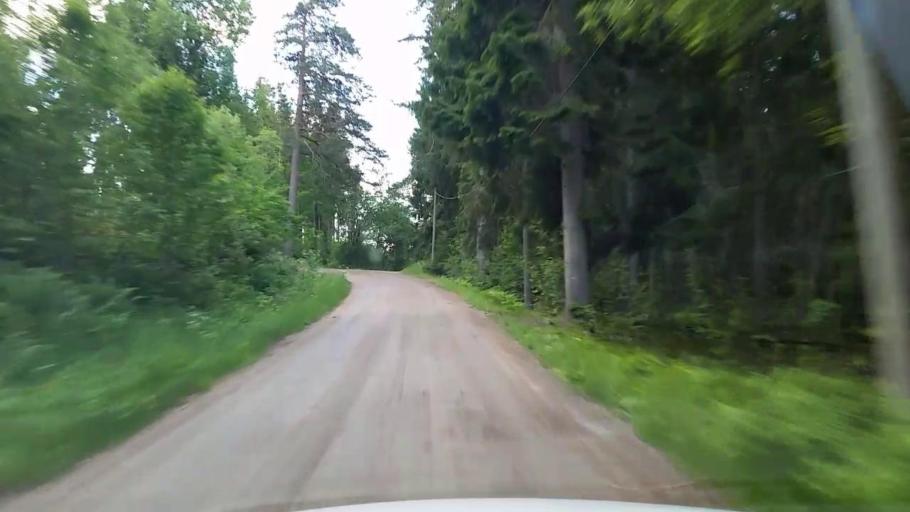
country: SE
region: Vaestmanland
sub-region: Kopings Kommun
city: Kolsva
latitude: 59.7770
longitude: 15.8698
